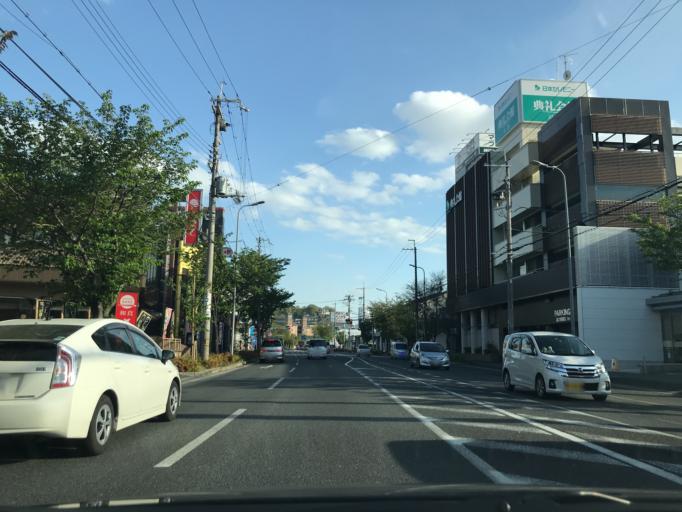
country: JP
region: Osaka
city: Ikeda
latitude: 34.8604
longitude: 135.4158
